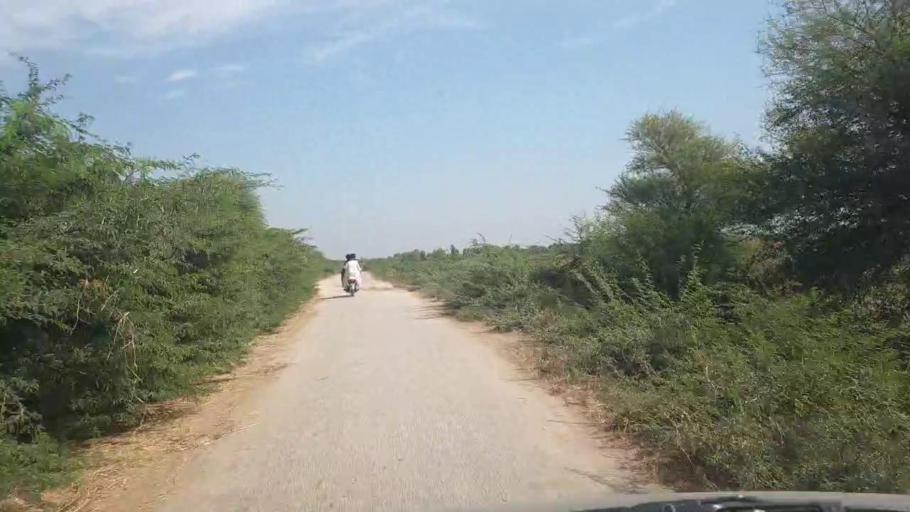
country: PK
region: Sindh
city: Tando Bago
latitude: 24.9163
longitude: 69.0448
